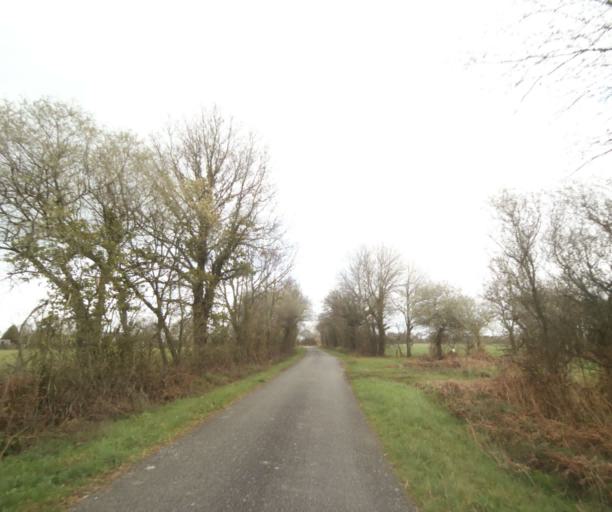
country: FR
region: Pays de la Loire
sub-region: Departement de la Loire-Atlantique
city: Bouvron
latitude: 47.4051
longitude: -1.8801
